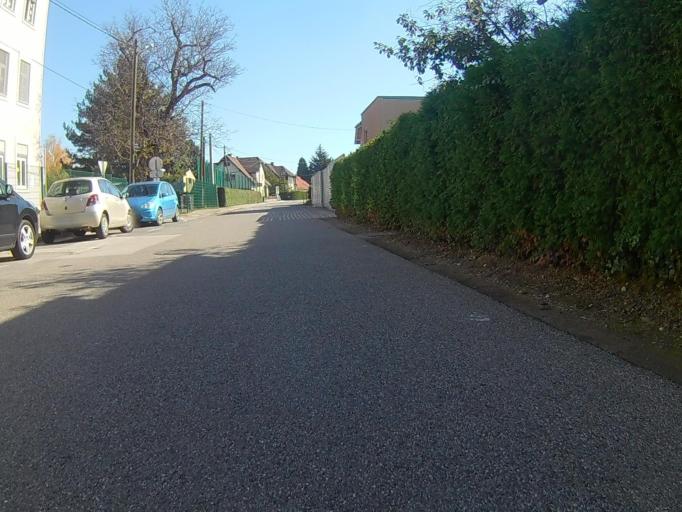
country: SI
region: Maribor
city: Maribor
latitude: 46.5558
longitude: 15.6716
